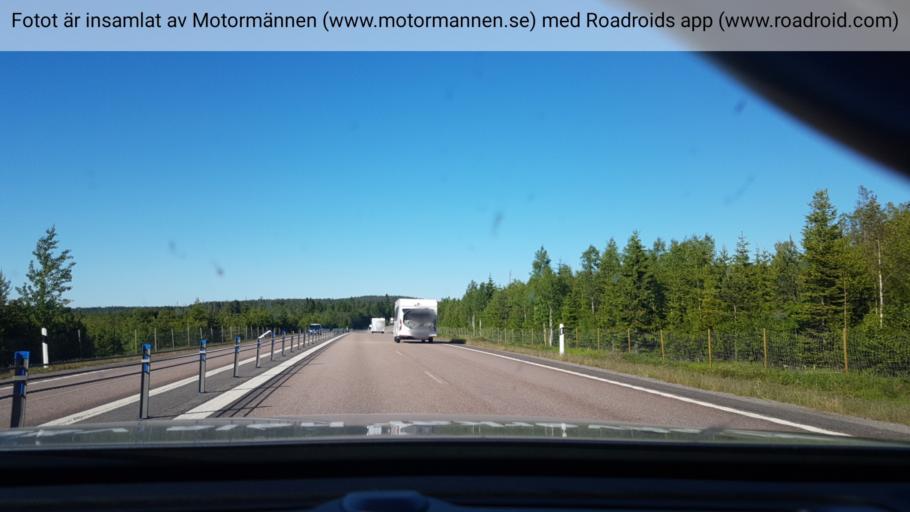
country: SE
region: Vaesternorrland
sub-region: Haernoesands Kommun
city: Haernoesand
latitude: 62.6030
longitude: 17.8159
